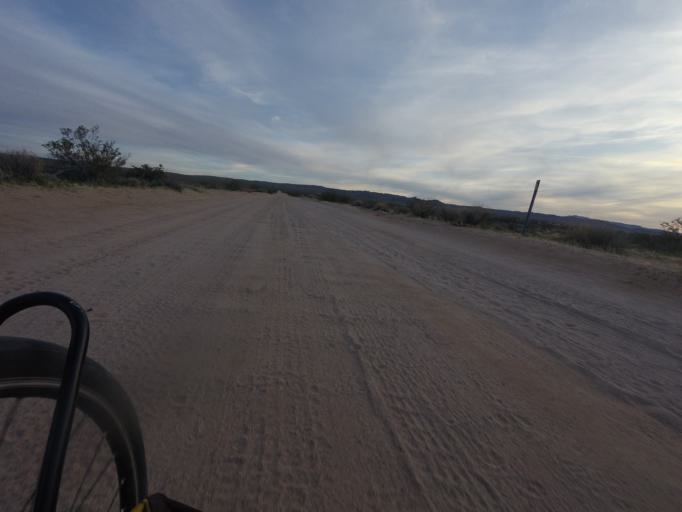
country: US
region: California
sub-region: Kern County
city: Ridgecrest
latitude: 35.6200
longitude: -117.6165
